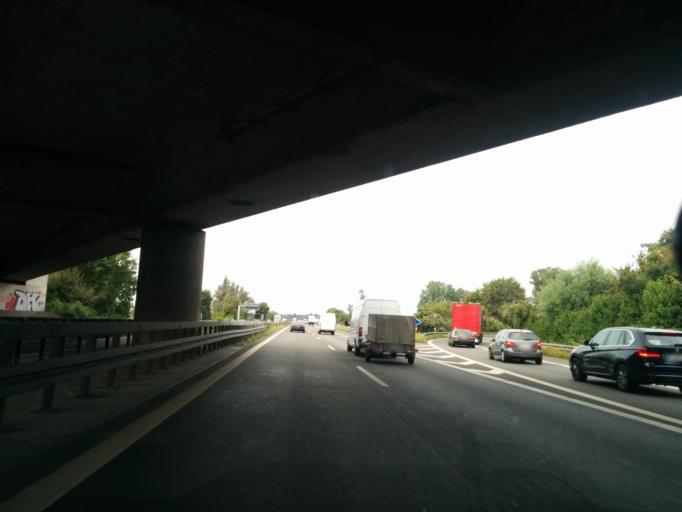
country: DE
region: Baden-Wuerttemberg
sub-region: Karlsruhe Region
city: Altlussheim
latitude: 49.3313
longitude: 8.5032
